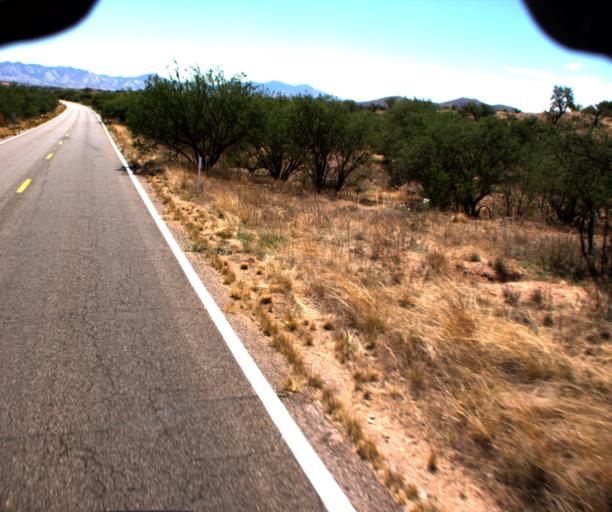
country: US
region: Arizona
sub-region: Santa Cruz County
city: Rio Rico
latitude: 31.4297
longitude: -110.9811
